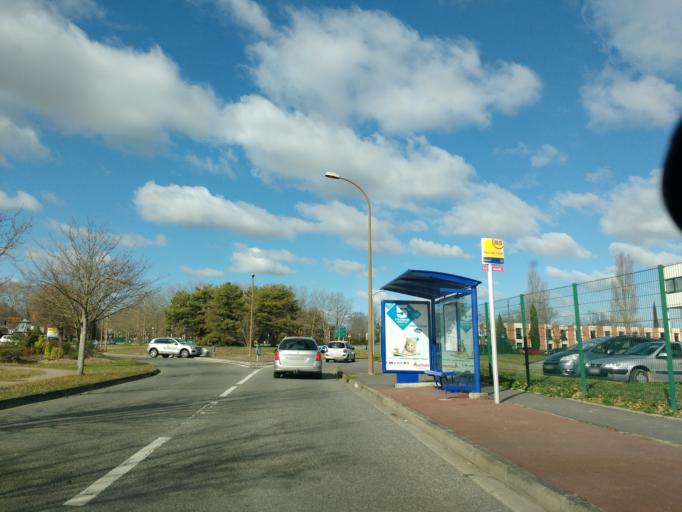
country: FR
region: Midi-Pyrenees
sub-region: Departement de la Haute-Garonne
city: Ramonville-Saint-Agne
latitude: 43.5535
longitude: 1.4849
